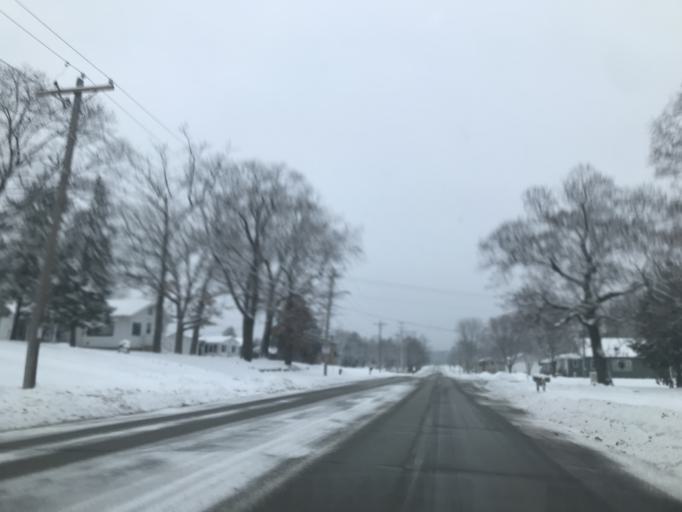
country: US
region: Wisconsin
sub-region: Oconto County
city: Oconto Falls
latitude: 44.8691
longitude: -88.1324
